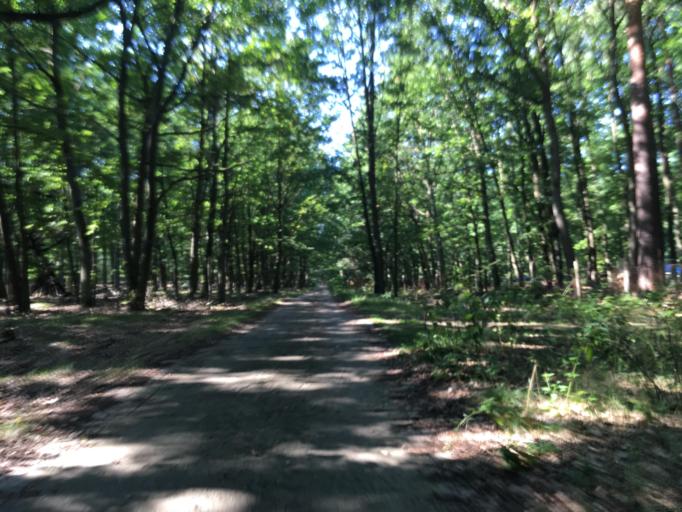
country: DE
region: Brandenburg
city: Gross Koris
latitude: 52.1961
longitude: 13.7326
